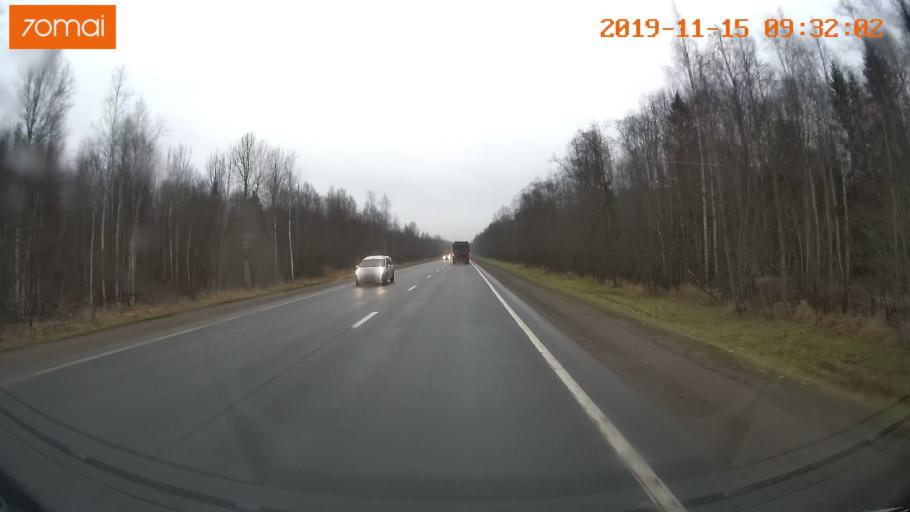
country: RU
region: Vologda
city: Sheksna
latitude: 59.2731
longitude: 38.3250
